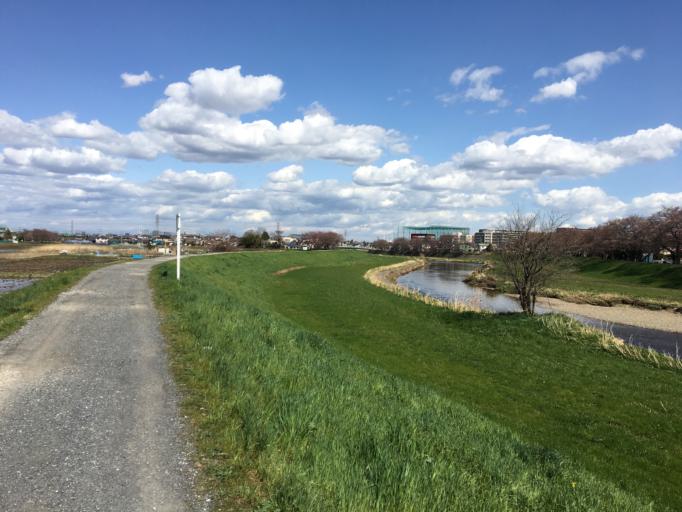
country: JP
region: Saitama
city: Shiki
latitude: 35.8348
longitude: 139.5681
